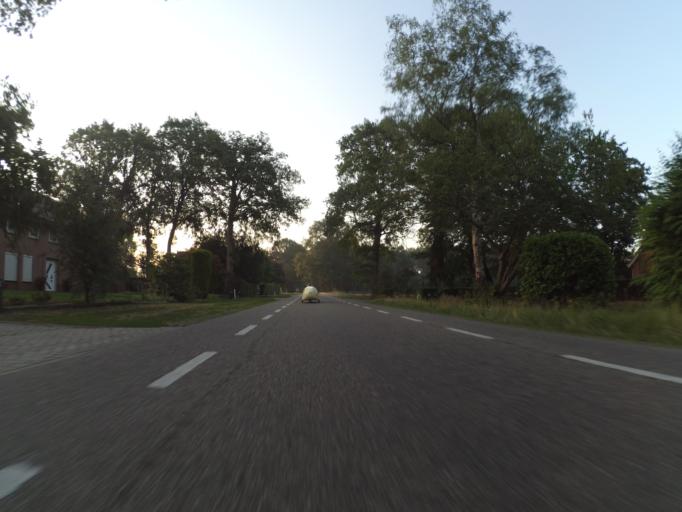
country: NL
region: Overijssel
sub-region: Gemeente Tubbergen
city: Tubbergen
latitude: 52.4024
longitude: 6.7947
